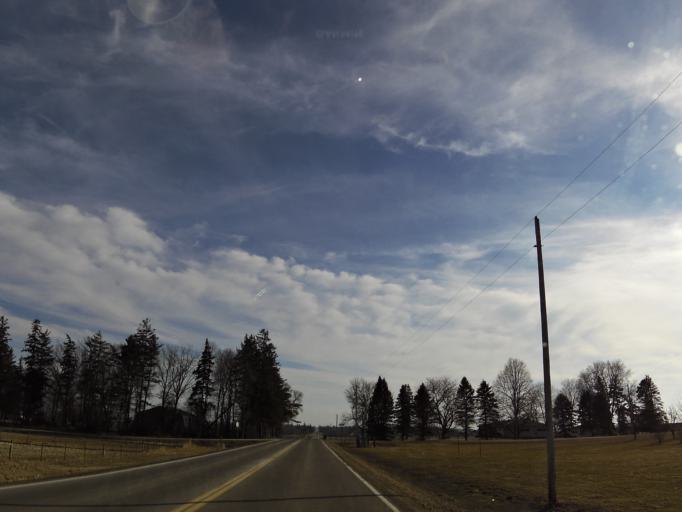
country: US
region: Minnesota
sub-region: Rice County
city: Northfield
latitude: 44.5306
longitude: -93.2010
